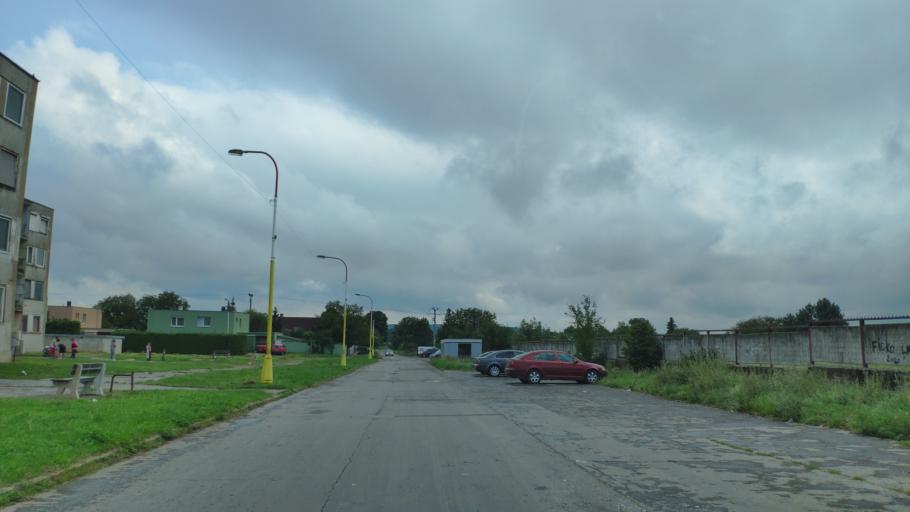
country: SK
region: Kosicky
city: Medzev
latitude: 48.5996
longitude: 20.8833
